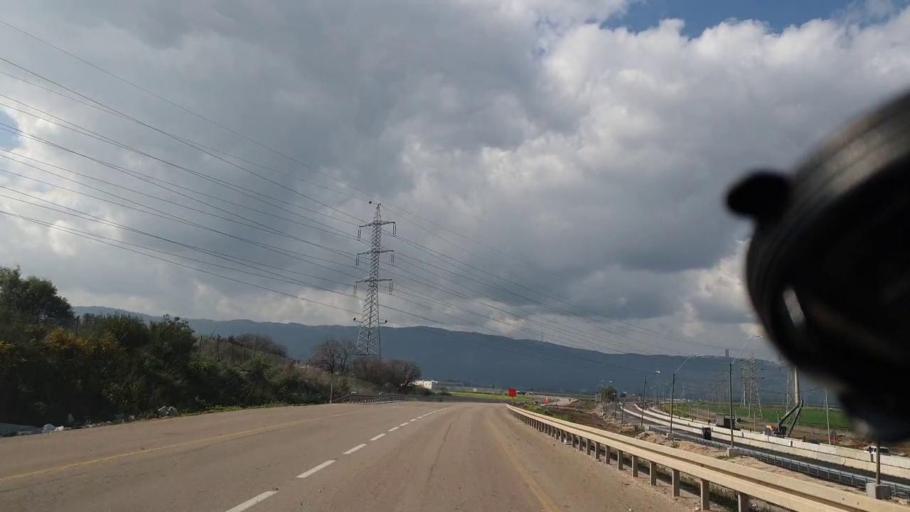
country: IL
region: Haifa
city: Ibtin
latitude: 32.7693
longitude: 35.1163
